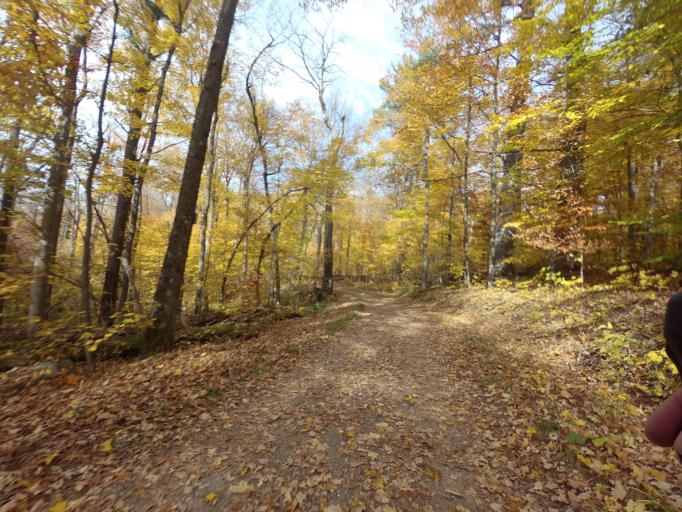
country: CA
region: Quebec
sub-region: Outaouais
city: Wakefield
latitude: 45.5046
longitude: -75.8750
